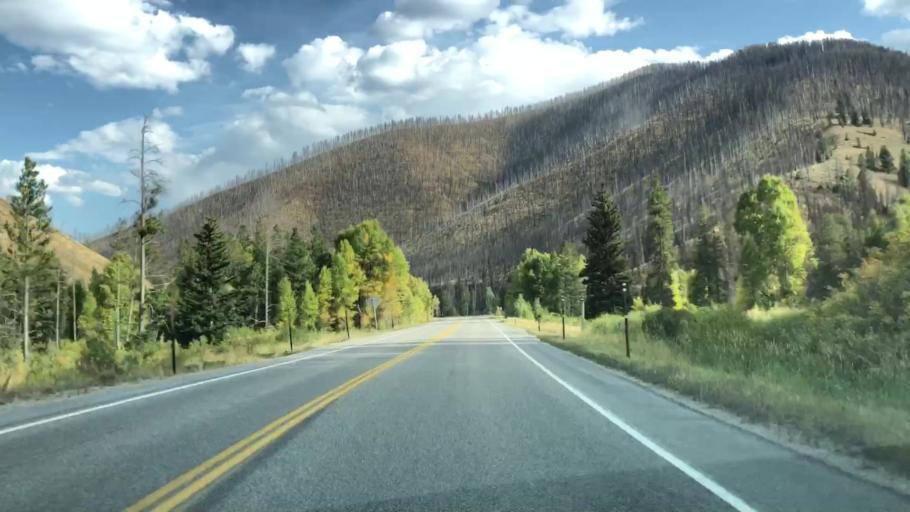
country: US
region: Wyoming
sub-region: Teton County
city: Hoback
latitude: 43.2505
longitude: -110.4961
